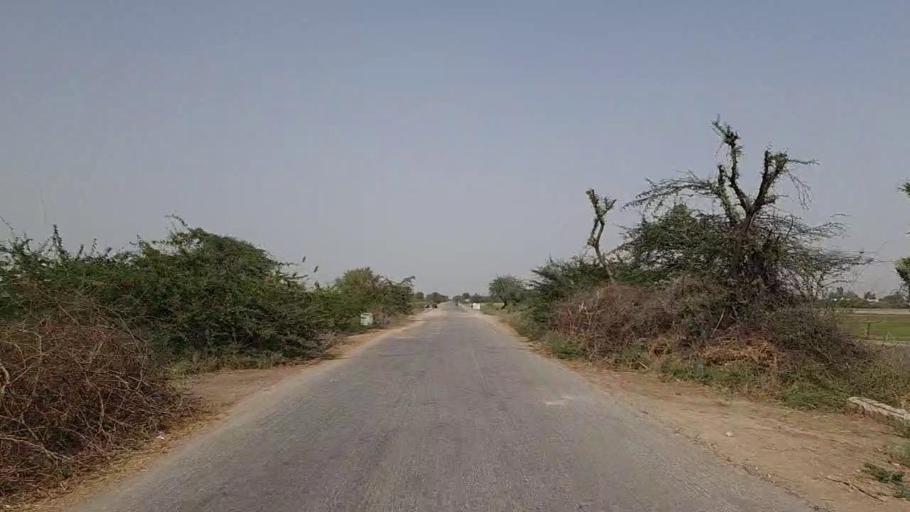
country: PK
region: Sindh
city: Tando Bago
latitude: 24.9008
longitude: 69.0829
